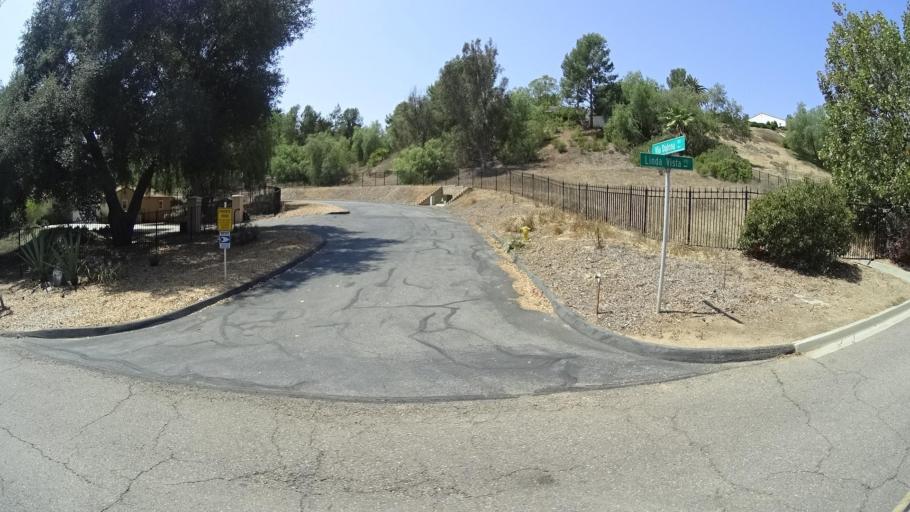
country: US
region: California
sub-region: San Diego County
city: Bonsall
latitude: 33.3198
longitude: -117.2090
